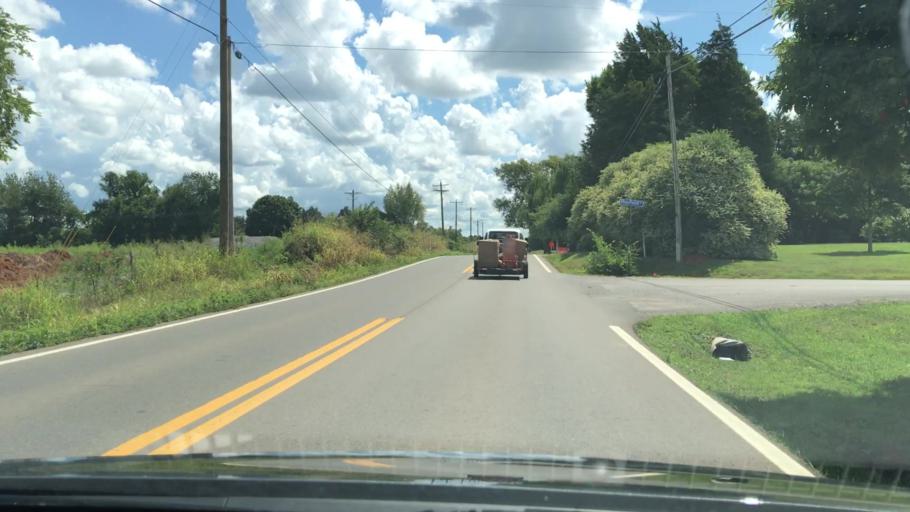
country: US
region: Tennessee
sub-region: Rutherford County
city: Smyrna
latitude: 35.8432
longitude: -86.5352
